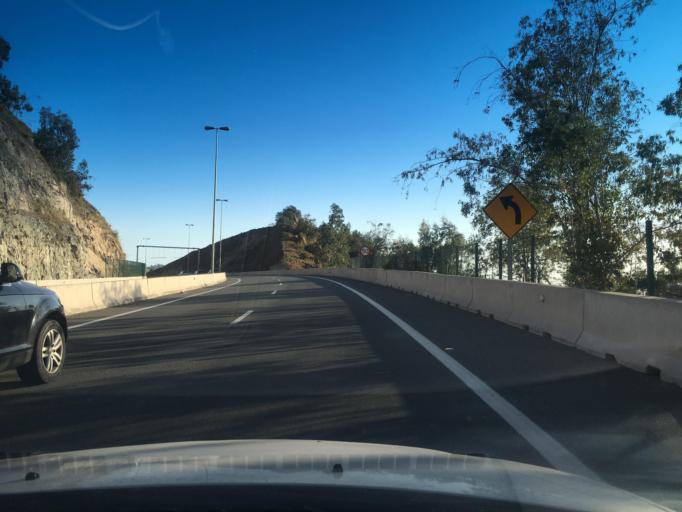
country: CL
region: Santiago Metropolitan
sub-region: Provincia de Santiago
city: Villa Presidente Frei, Nunoa, Santiago, Chile
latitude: -33.3812
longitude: -70.6035
